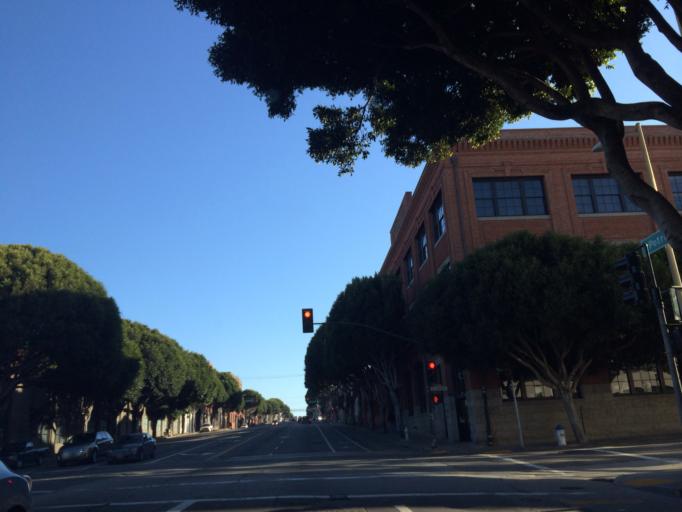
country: US
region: California
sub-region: San Francisco County
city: San Francisco
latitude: 37.7686
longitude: -122.4079
